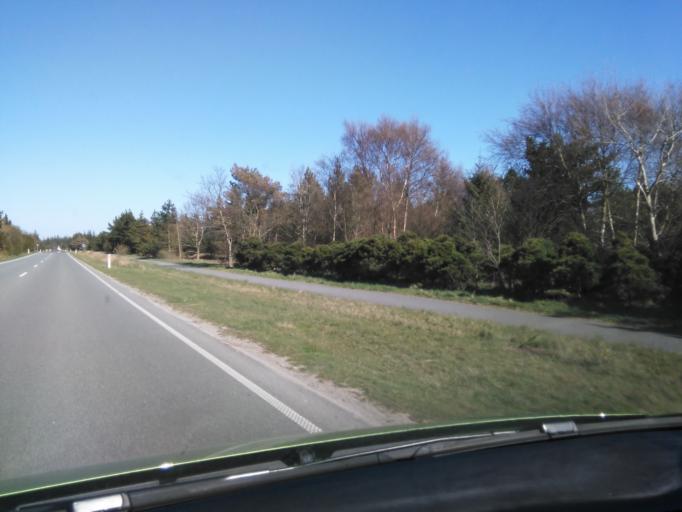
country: DK
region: South Denmark
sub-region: Varde Kommune
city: Oksbol
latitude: 55.5593
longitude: 8.1572
